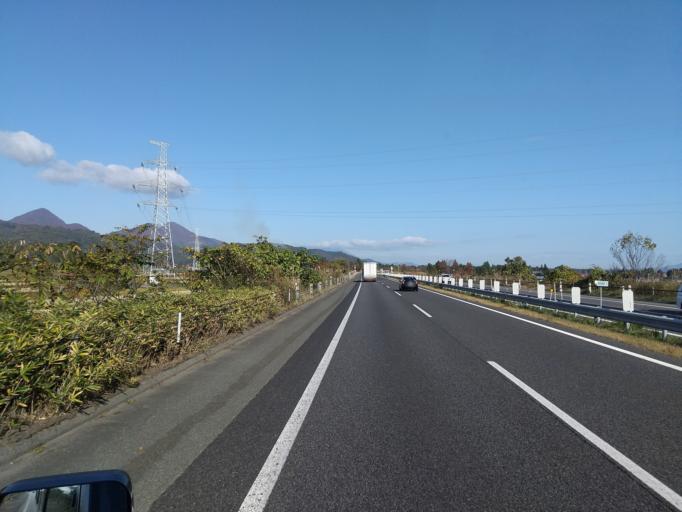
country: JP
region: Iwate
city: Morioka-shi
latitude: 39.5801
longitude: 141.1198
